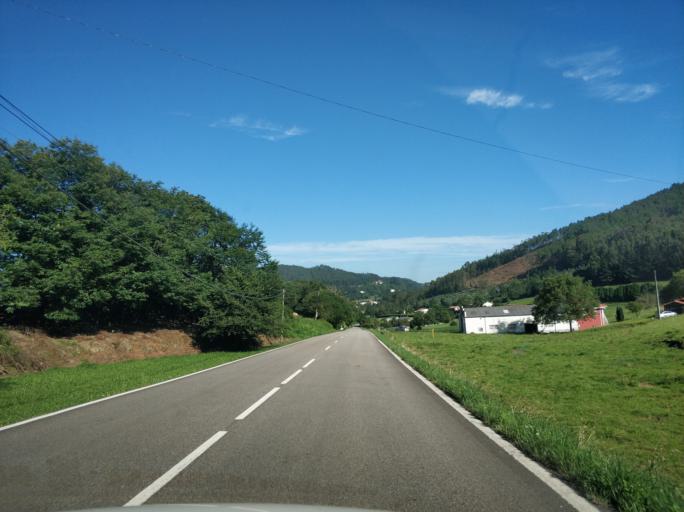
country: ES
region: Asturias
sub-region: Province of Asturias
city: Cudillero
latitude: 43.5473
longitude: -6.2211
